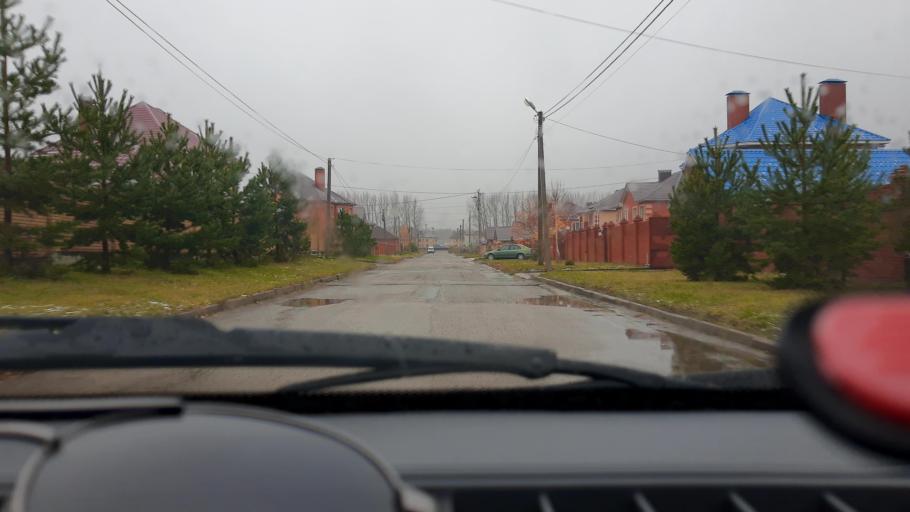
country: RU
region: Bashkortostan
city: Kabakovo
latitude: 54.6214
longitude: 56.1224
